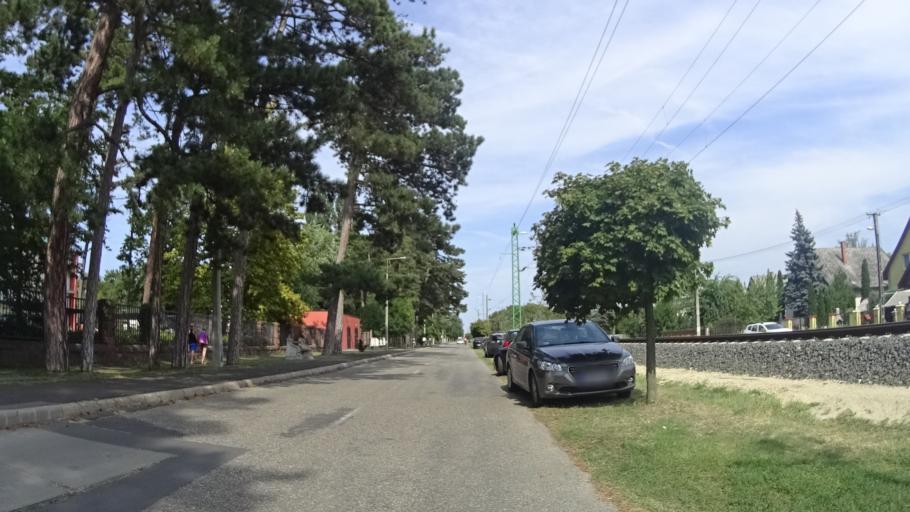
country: HU
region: Somogy
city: Balatonlelle
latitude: 46.7918
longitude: 17.7095
